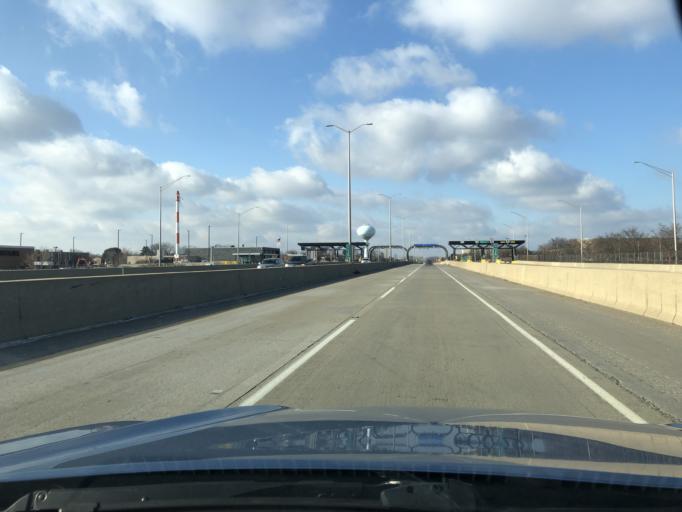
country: US
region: Illinois
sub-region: Lake County
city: Deerfield
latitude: 42.1497
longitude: -87.8524
